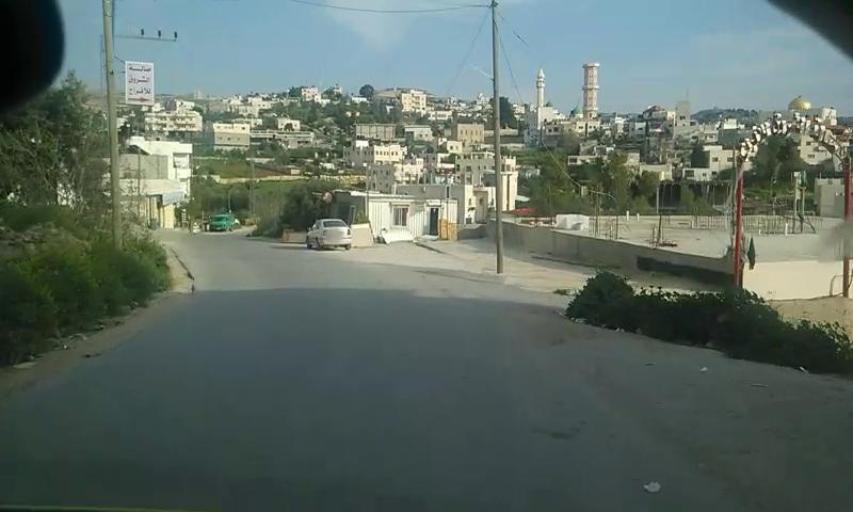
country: PS
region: West Bank
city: Nuba
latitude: 31.6095
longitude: 35.0349
